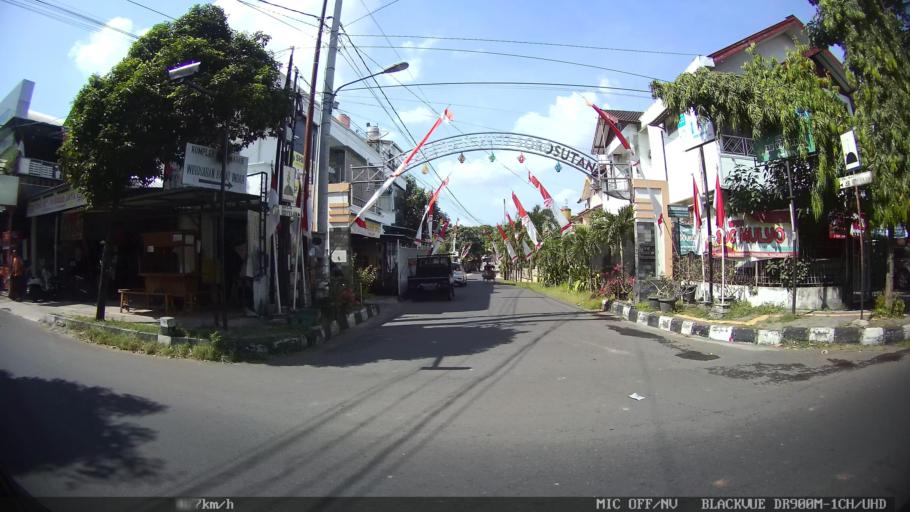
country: ID
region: Daerah Istimewa Yogyakarta
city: Yogyakarta
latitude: -7.8255
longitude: 110.3755
